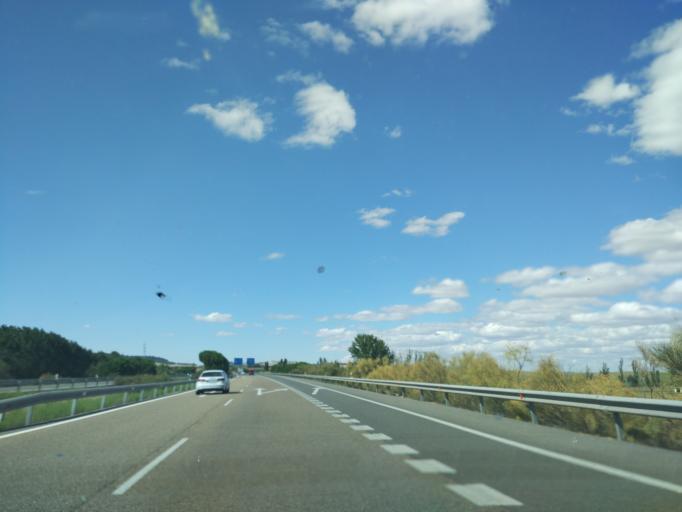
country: ES
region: Castille and Leon
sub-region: Provincia de Valladolid
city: Tordesillas
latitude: 41.4961
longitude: -4.9831
